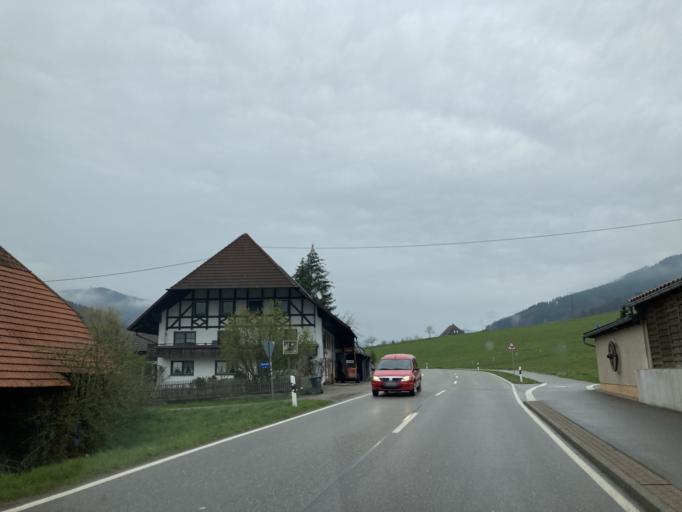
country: DE
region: Baden-Wuerttemberg
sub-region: Freiburg Region
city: Elzach
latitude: 48.1888
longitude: 8.0949
